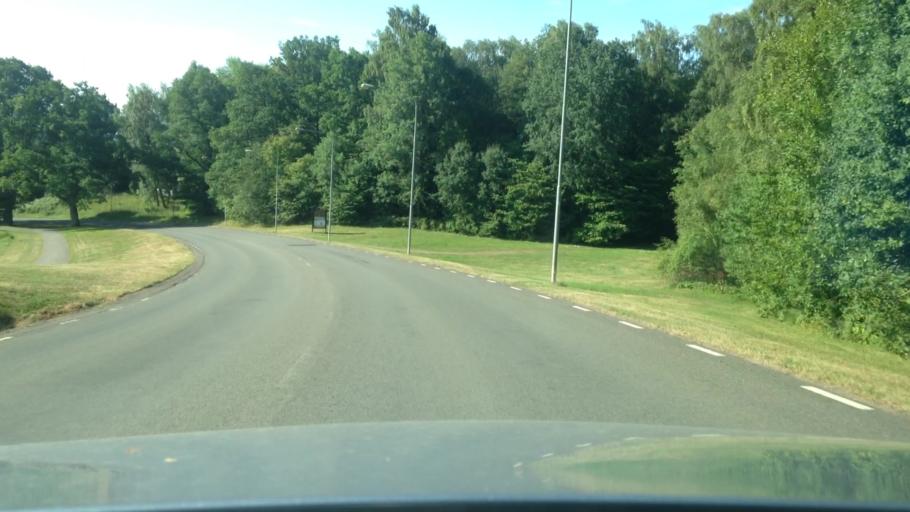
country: SE
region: Vaestra Goetaland
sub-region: Skovde Kommun
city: Skoevde
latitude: 58.3976
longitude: 13.8184
